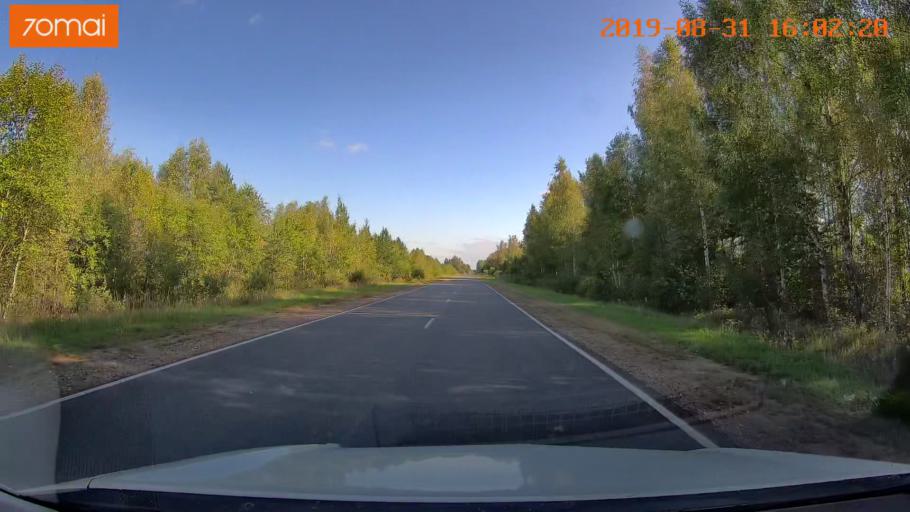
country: RU
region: Kaluga
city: Yukhnov
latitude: 54.6766
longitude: 35.3008
